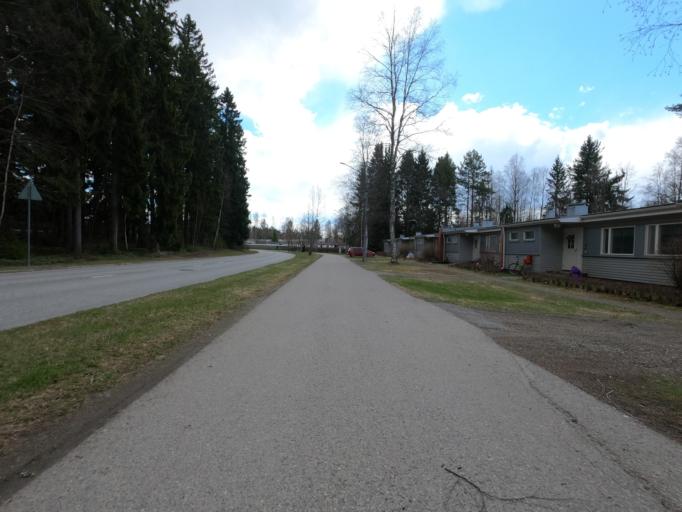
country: FI
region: North Karelia
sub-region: Joensuu
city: Joensuu
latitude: 62.5844
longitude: 29.7783
